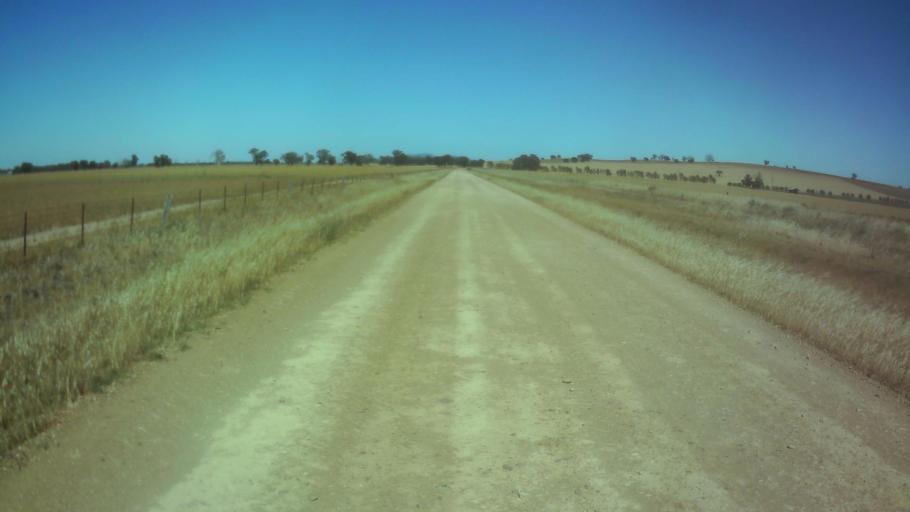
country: AU
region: New South Wales
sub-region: Weddin
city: Grenfell
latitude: -33.9956
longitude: 148.3685
